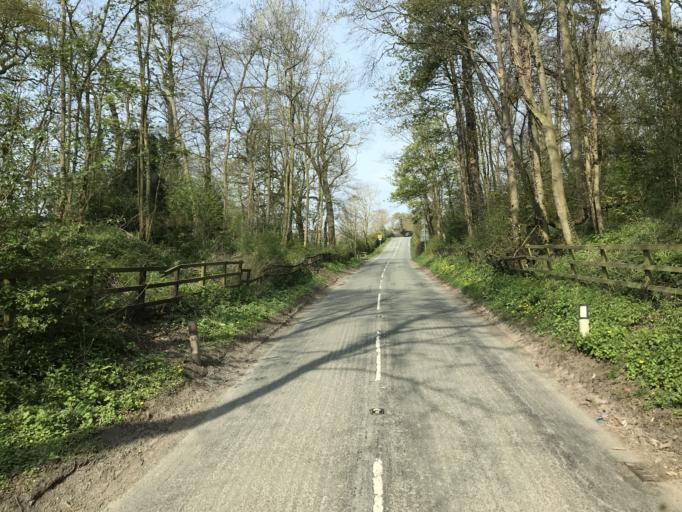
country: GB
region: England
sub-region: Cheshire West and Chester
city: Aldford
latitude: 53.1358
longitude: -2.8655
